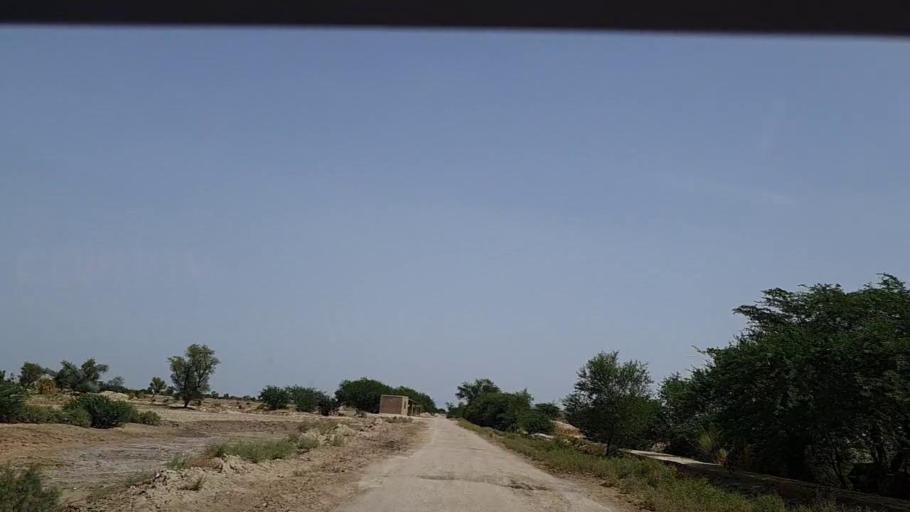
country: PK
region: Sindh
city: Johi
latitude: 26.7743
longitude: 67.6253
